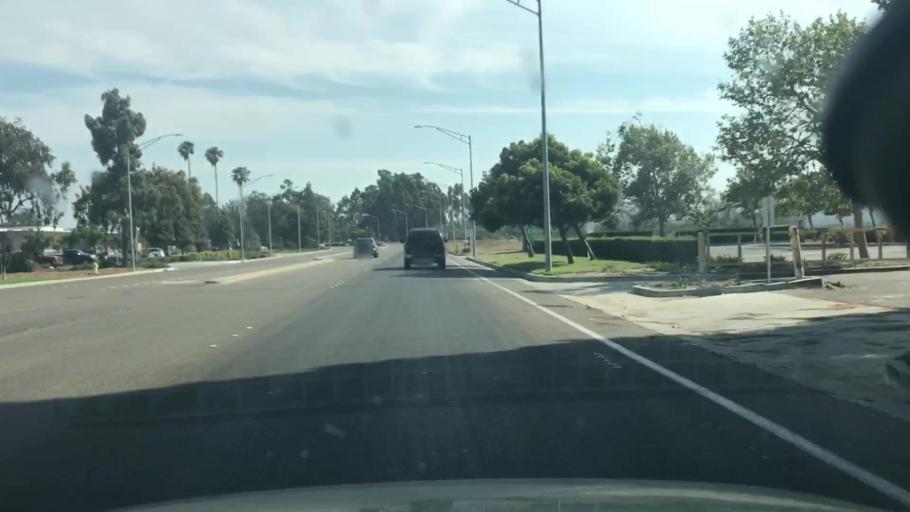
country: US
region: California
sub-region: Santa Barbara County
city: Santa Maria
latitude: 34.9103
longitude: -120.4542
